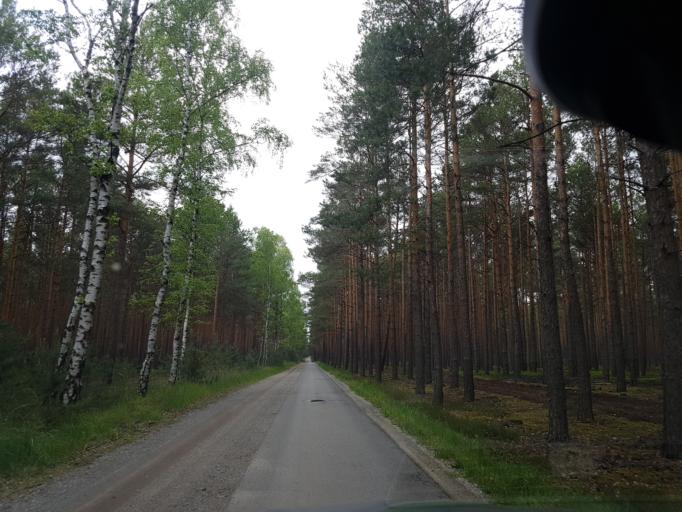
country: DE
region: Brandenburg
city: Crinitz
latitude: 51.6889
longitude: 13.7773
